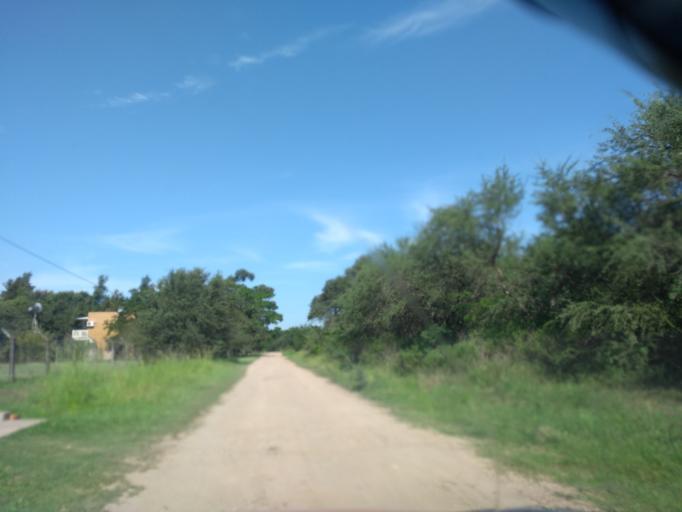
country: AR
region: Chaco
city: Barranqueras
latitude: -27.4315
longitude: -58.9387
